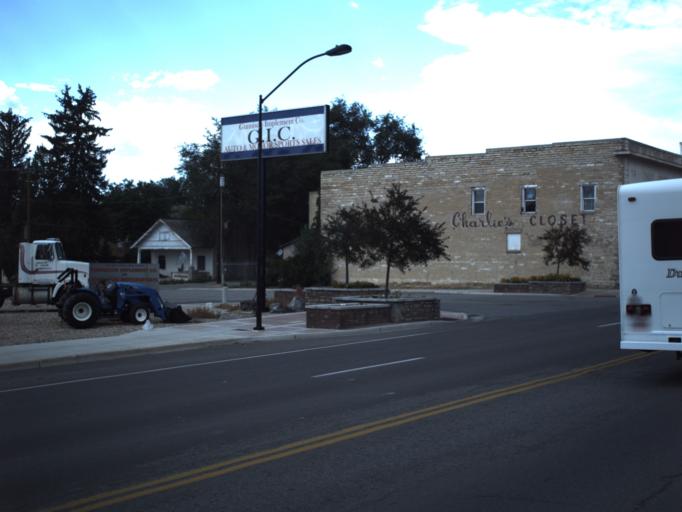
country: US
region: Utah
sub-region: Sanpete County
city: Gunnison
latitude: 39.1533
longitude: -111.8183
